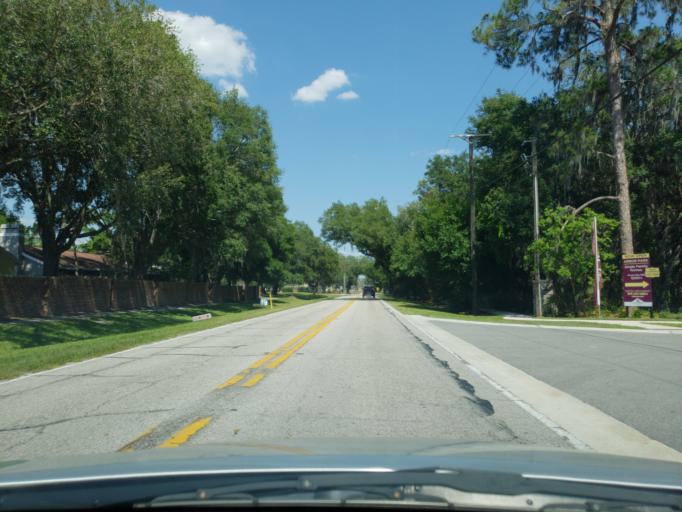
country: US
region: Florida
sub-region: Hillsborough County
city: Riverview
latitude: 27.8717
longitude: -82.3329
